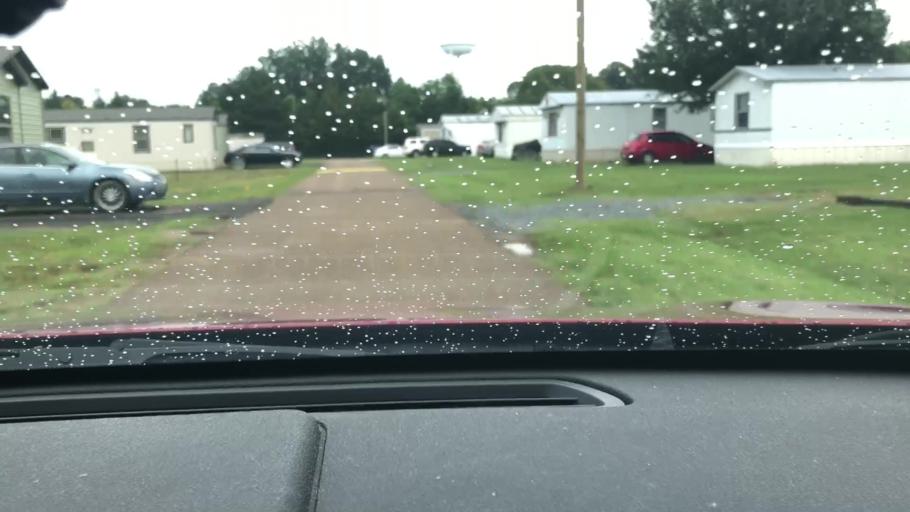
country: US
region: Texas
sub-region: Bowie County
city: Nash
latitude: 33.4445
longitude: -94.1378
